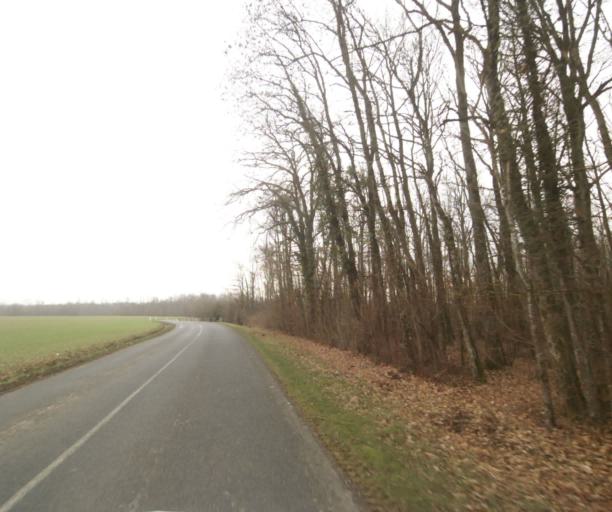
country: FR
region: Champagne-Ardenne
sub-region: Departement de la Marne
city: Pargny-sur-Saulx
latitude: 48.7384
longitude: 4.8565
